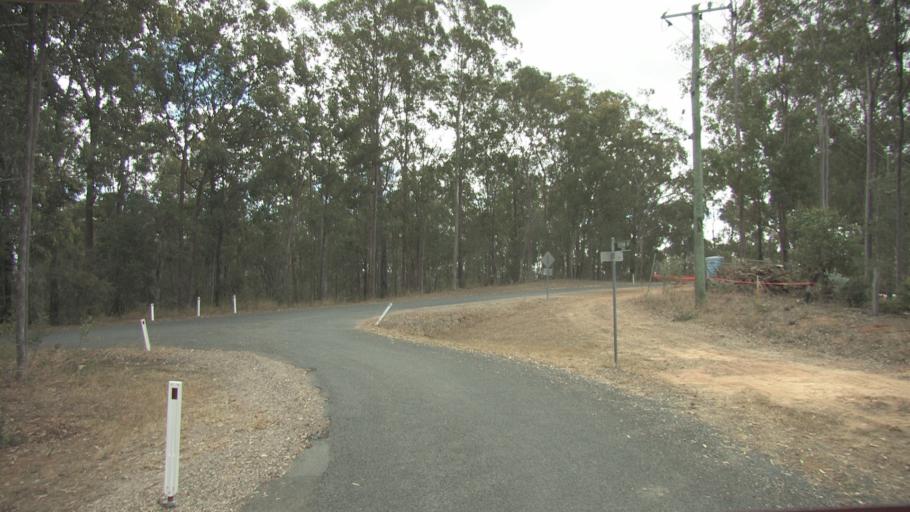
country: AU
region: Queensland
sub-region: Logan
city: Cedar Vale
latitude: -27.8996
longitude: 153.0376
